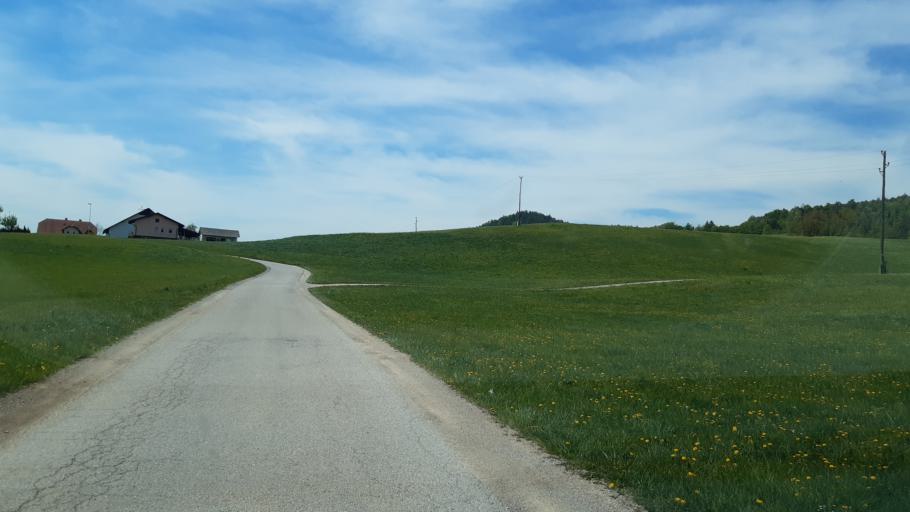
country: SI
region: Lukovica
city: Lukovica pri Domzalah
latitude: 46.1772
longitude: 14.6603
